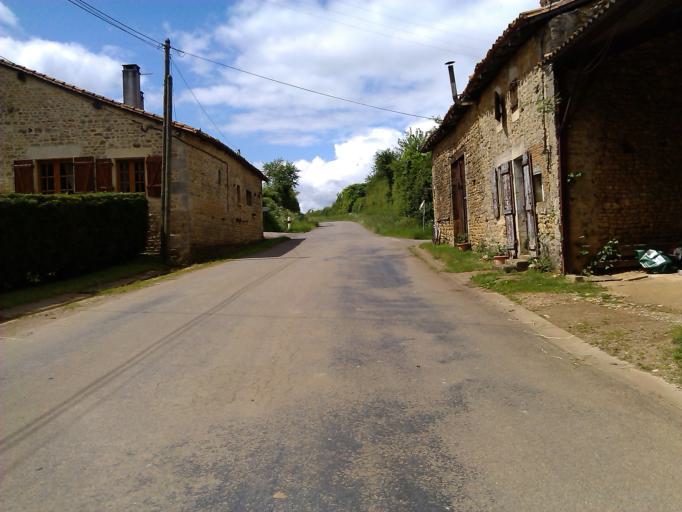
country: FR
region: Poitou-Charentes
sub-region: Departement de la Charente
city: Champagne-Mouton
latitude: 46.0708
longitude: 0.4917
